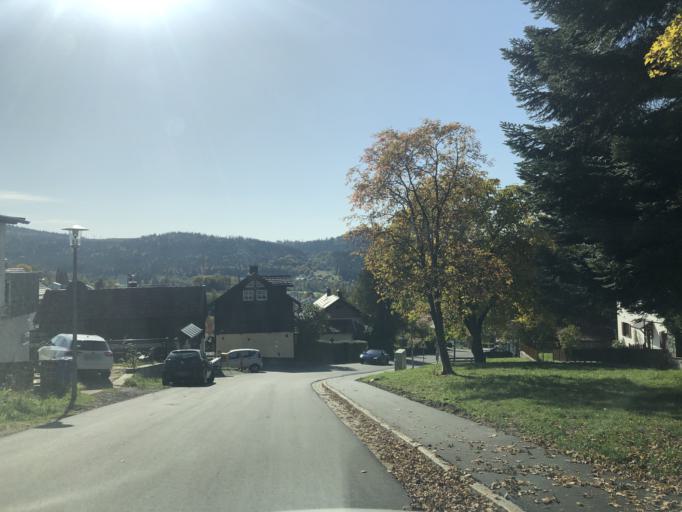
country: DE
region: Bavaria
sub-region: Lower Bavaria
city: Bodenmais
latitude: 49.0705
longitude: 13.1082
